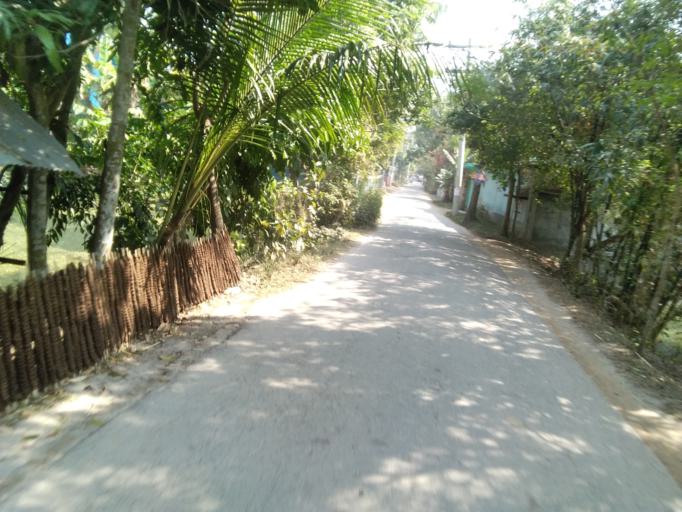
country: IN
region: West Bengal
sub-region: North 24 Parganas
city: Taki
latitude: 22.5906
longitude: 88.9965
